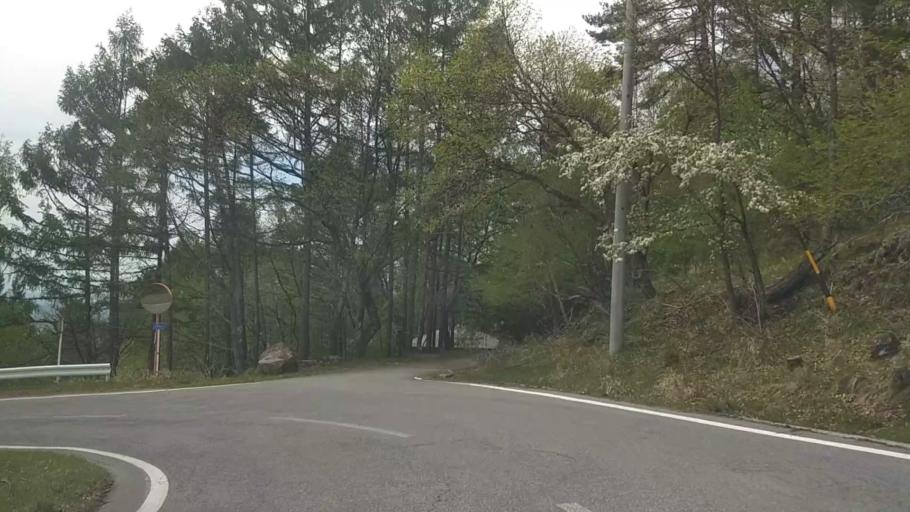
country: JP
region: Nagano
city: Chino
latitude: 36.0469
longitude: 138.2745
